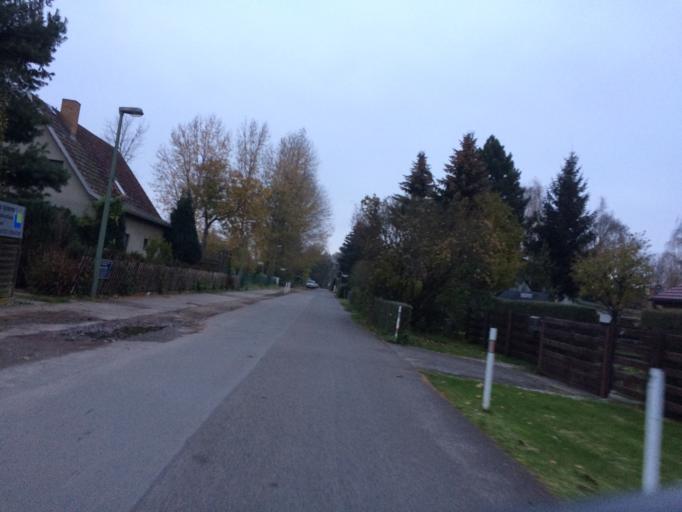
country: DE
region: Berlin
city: Weissensee
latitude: 52.5711
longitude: 13.4642
